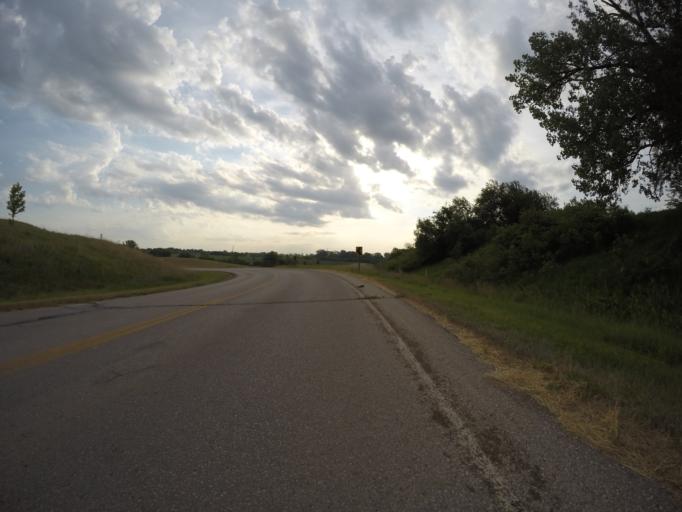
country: US
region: Kansas
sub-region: Doniphan County
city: Troy
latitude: 39.7917
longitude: -95.0762
